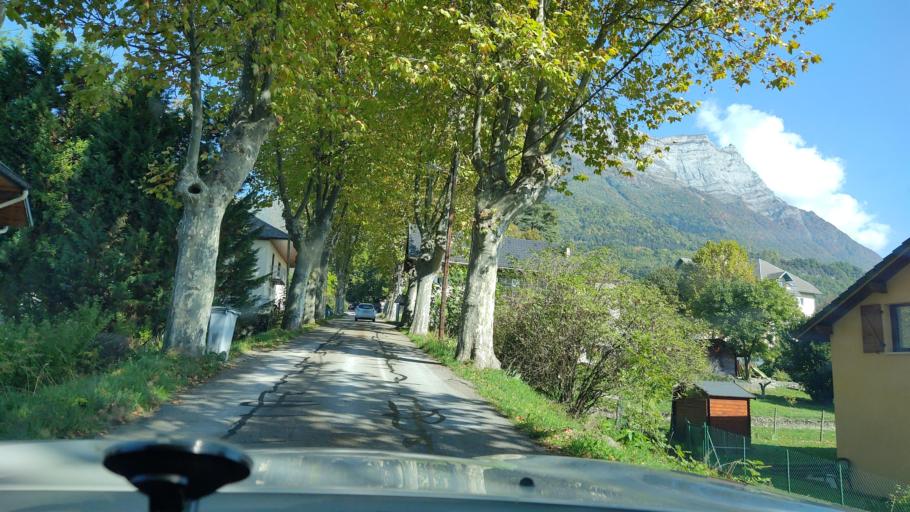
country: FR
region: Rhone-Alpes
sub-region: Departement de la Savoie
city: Coise-Saint-Jean-Pied-Gauthier
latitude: 45.5666
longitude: 6.1544
